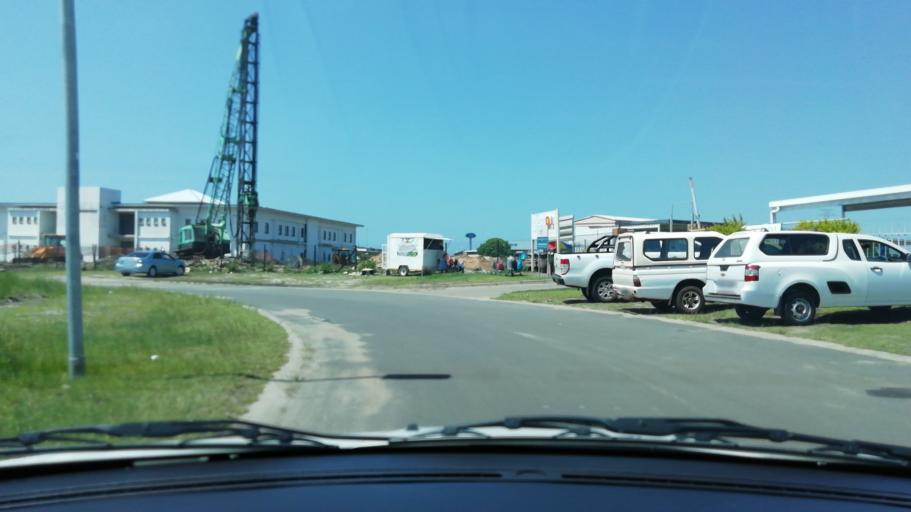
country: ZA
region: KwaZulu-Natal
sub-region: uThungulu District Municipality
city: Richards Bay
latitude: -28.7414
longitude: 32.0503
